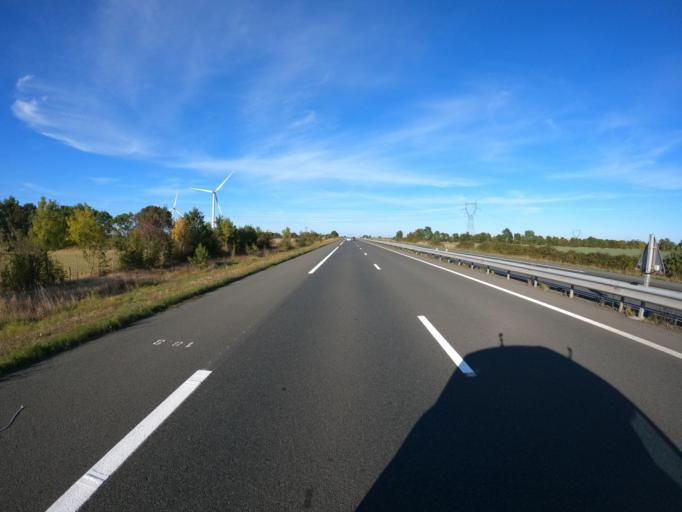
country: FR
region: Pays de la Loire
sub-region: Departement de Maine-et-Loire
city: Saint-Lambert-du-Lattay
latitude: 47.2520
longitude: -0.6230
